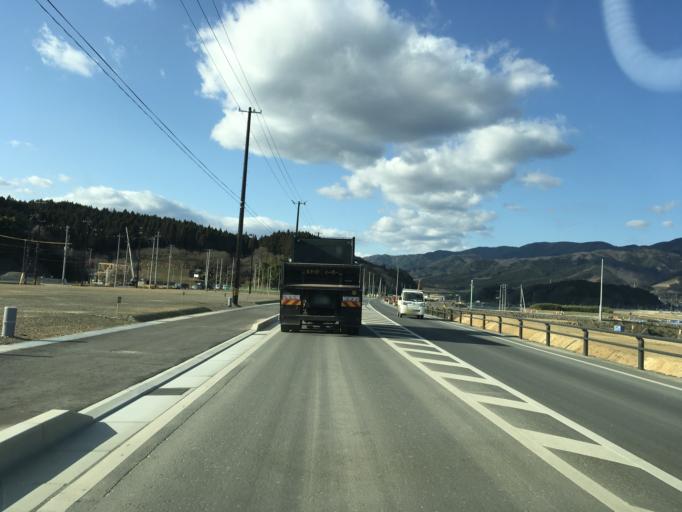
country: JP
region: Iwate
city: Ofunato
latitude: 39.0084
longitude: 141.6165
